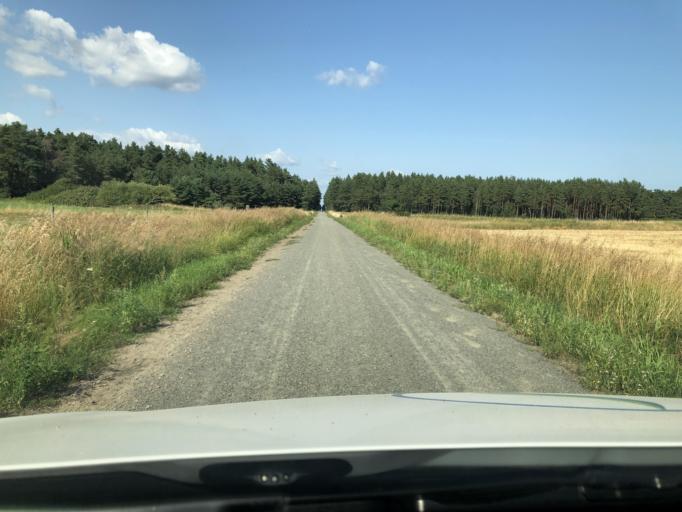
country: SE
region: Skane
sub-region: Kristianstads Kommun
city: Norra Asum
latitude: 55.9136
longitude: 14.1157
